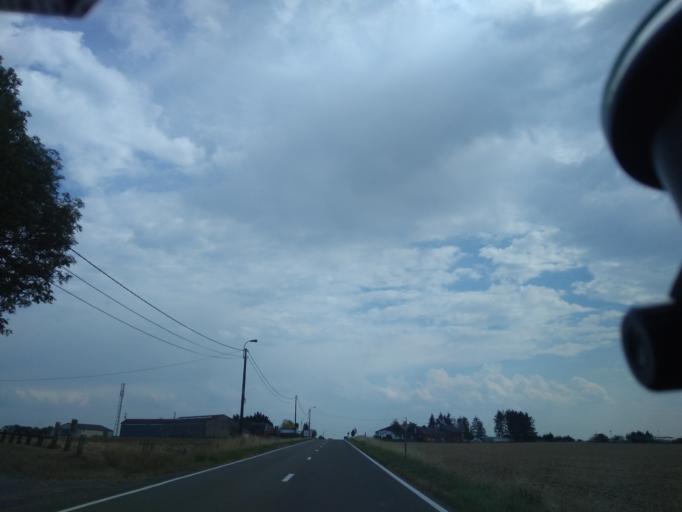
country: BE
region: Wallonia
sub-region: Province de Namur
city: Beauraing
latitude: 50.1582
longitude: 4.9165
